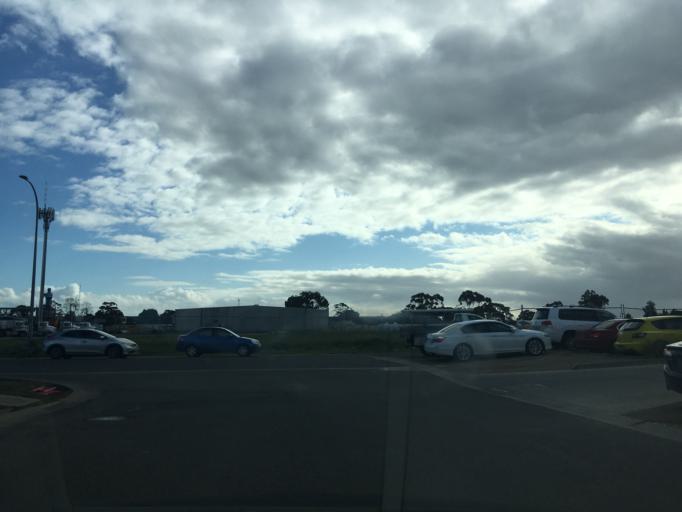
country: AU
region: Victoria
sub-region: Wyndham
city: Hoppers Crossing
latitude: -37.8727
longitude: 144.7171
